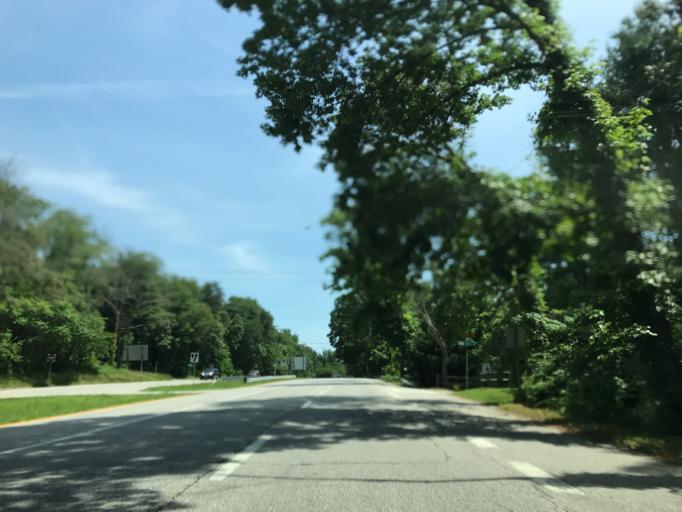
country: US
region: Maryland
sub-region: Anne Arundel County
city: Naval Academy
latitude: 39.0079
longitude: -76.4869
